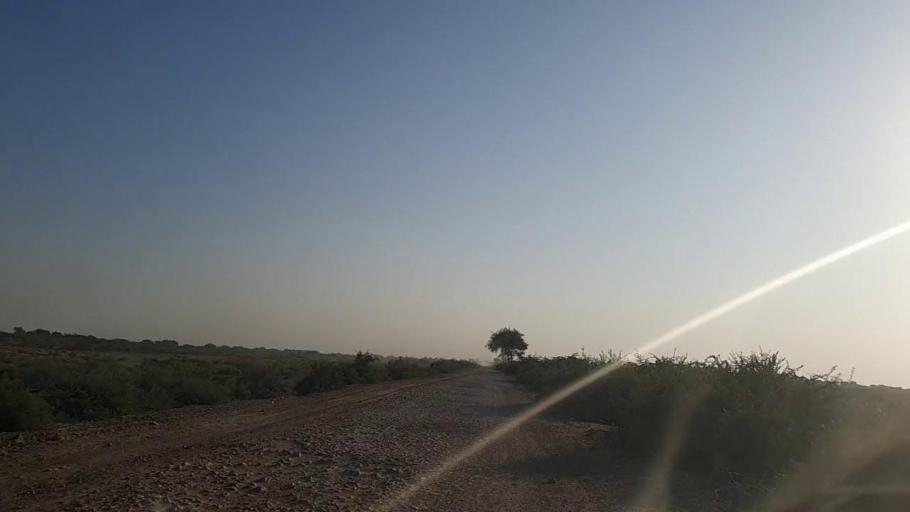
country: PK
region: Sindh
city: Jati
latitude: 24.4421
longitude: 68.1945
